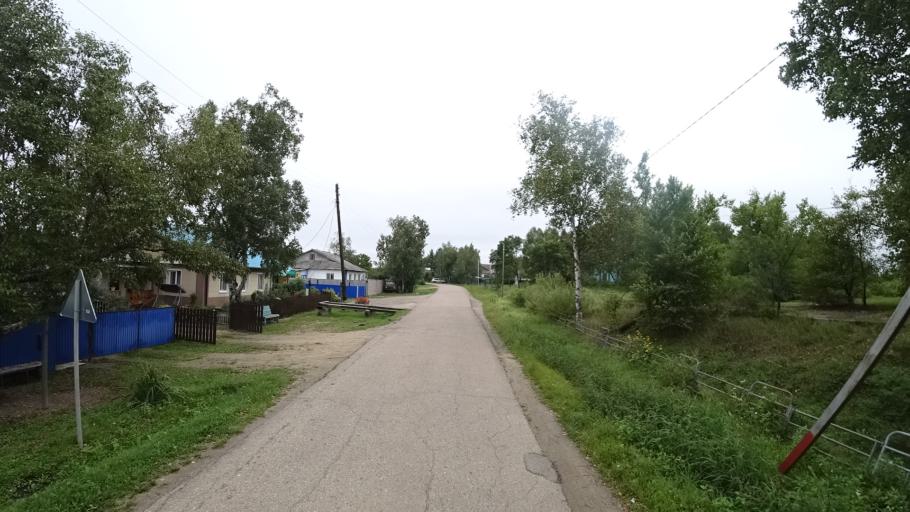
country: RU
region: Primorskiy
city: Monastyrishche
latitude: 44.0826
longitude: 132.5816
